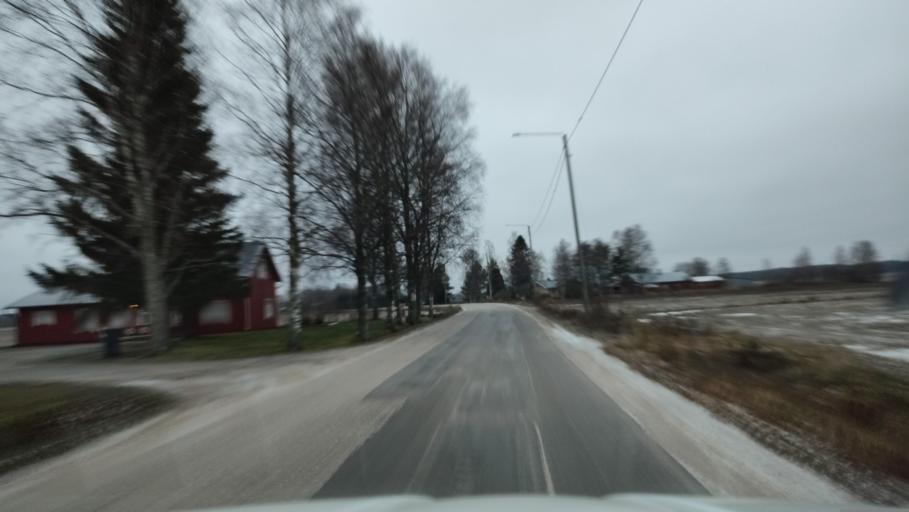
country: FI
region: Southern Ostrobothnia
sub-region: Suupohja
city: Karijoki
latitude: 62.2698
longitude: 21.6866
